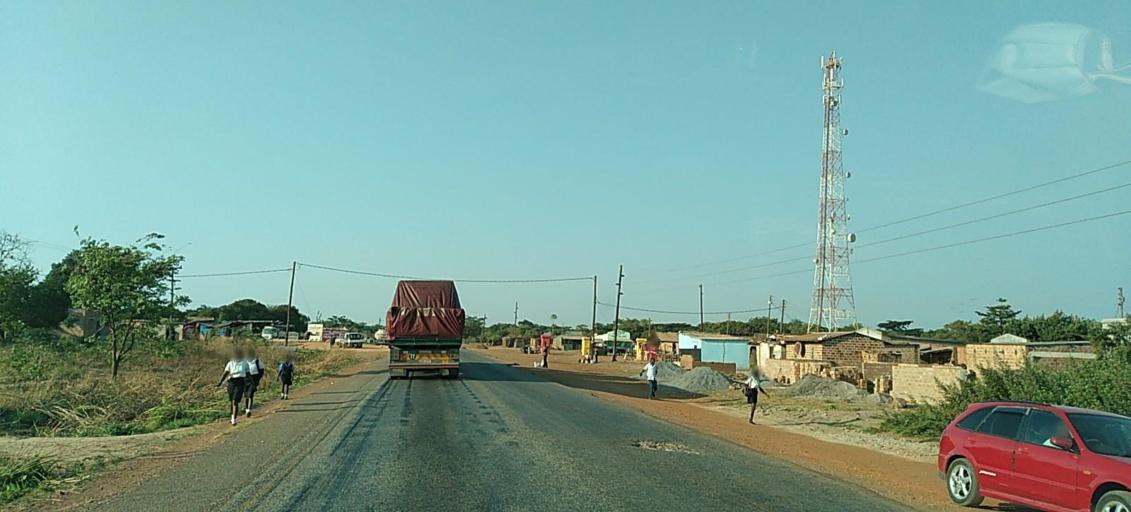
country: ZM
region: Copperbelt
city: Luanshya
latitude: -13.4694
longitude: 28.6737
